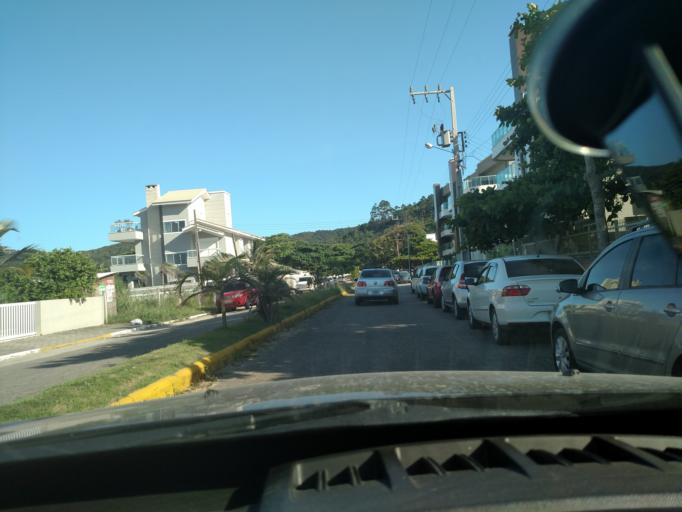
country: BR
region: Santa Catarina
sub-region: Porto Belo
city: Porto Belo
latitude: -27.1958
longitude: -48.4975
